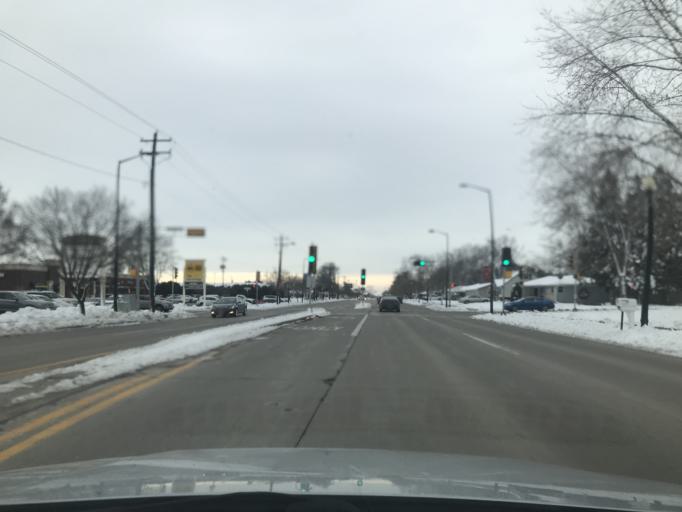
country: US
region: Wisconsin
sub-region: Brown County
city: Ashwaubenon
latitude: 44.4961
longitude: -88.0607
